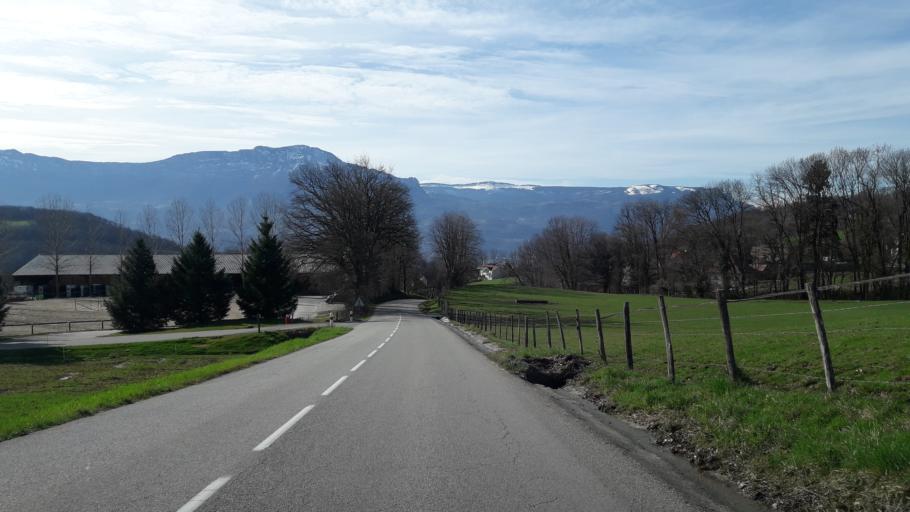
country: FR
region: Rhone-Alpes
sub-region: Departement de l'Isere
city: Herbeys
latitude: 45.1395
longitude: 5.7868
